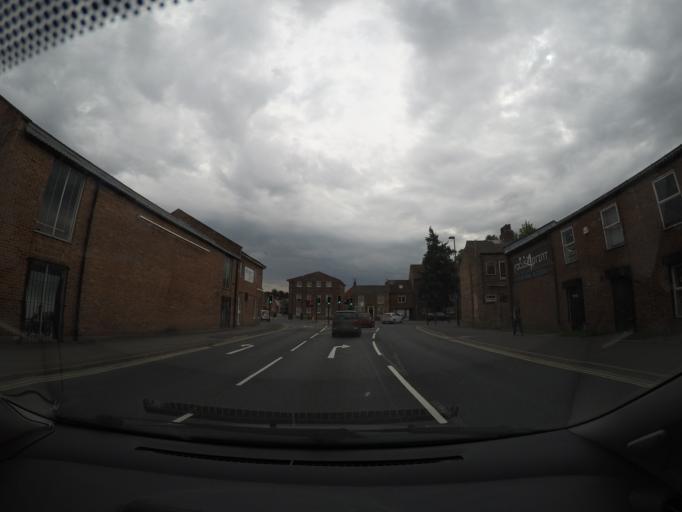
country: GB
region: England
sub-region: City of York
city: York
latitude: 53.9550
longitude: -1.0675
